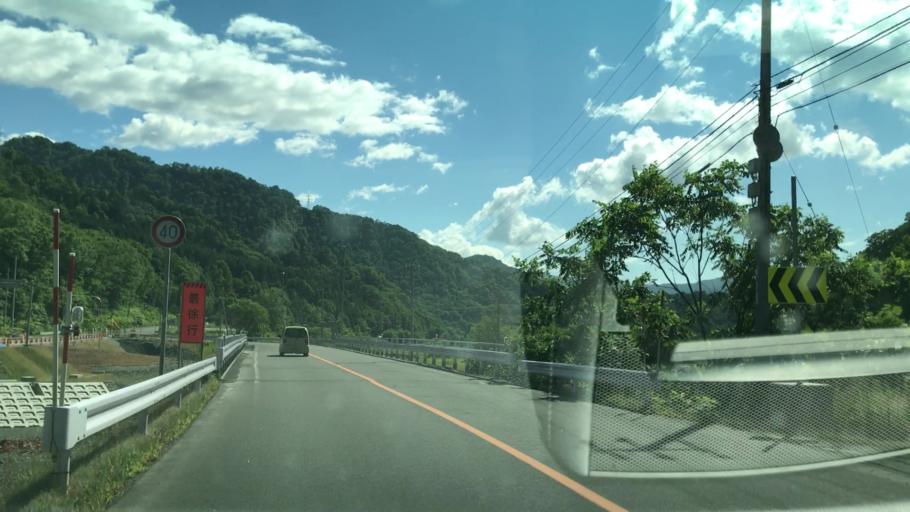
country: JP
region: Hokkaido
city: Shimo-furano
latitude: 42.9116
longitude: 142.5857
